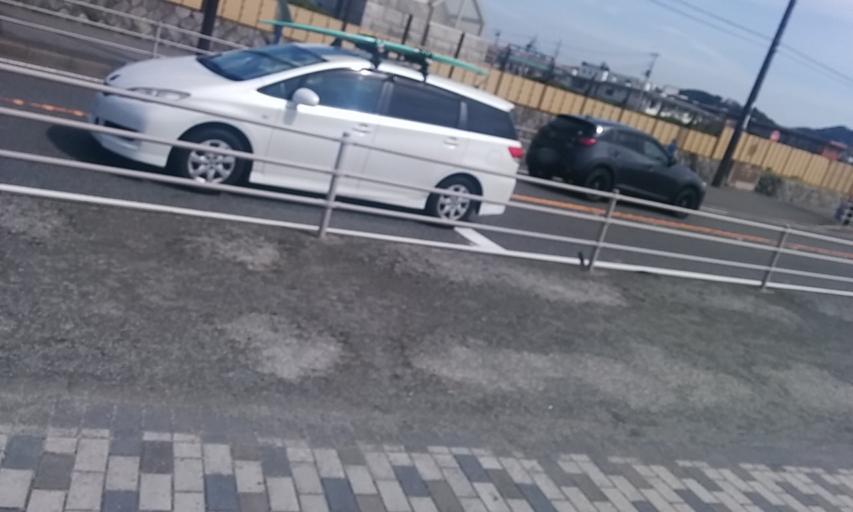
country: JP
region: Kanagawa
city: Kamakura
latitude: 35.3096
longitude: 139.5429
